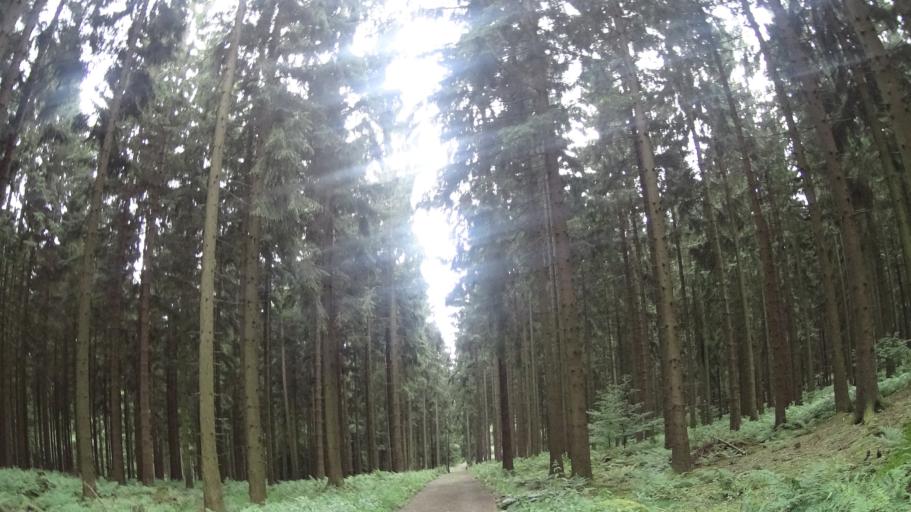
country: DE
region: Lower Saxony
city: Bad Munder am Deister
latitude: 52.1807
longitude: 9.4012
